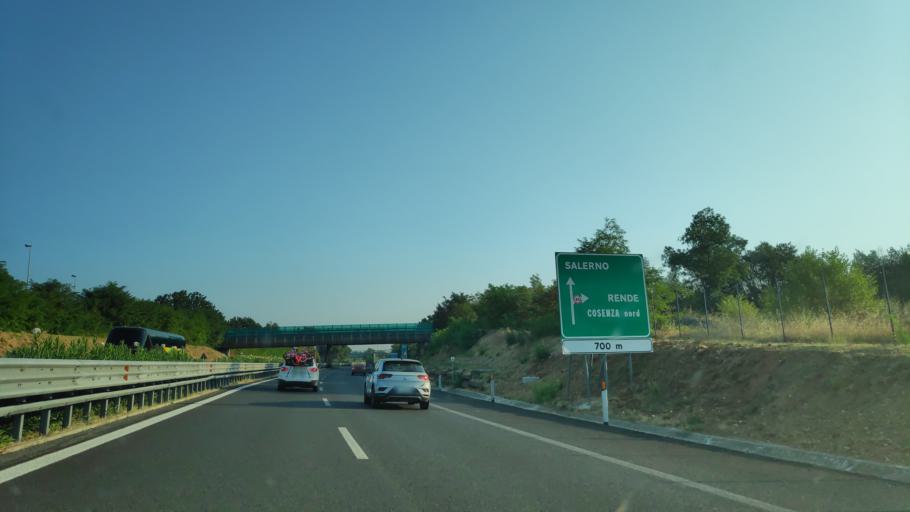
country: IT
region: Calabria
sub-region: Provincia di Cosenza
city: Quattromiglia
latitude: 39.3414
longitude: 16.2347
